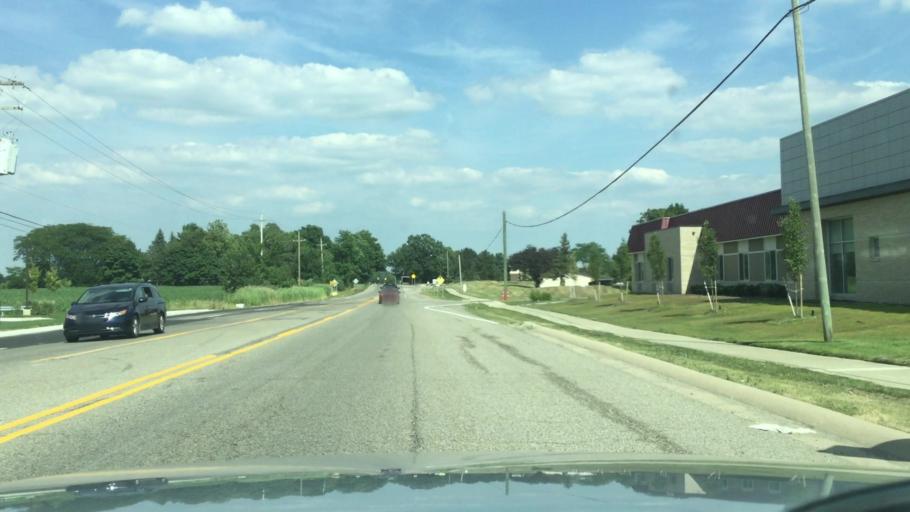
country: US
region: Michigan
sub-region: Genesee County
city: Grand Blanc
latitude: 42.9309
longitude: -83.5961
